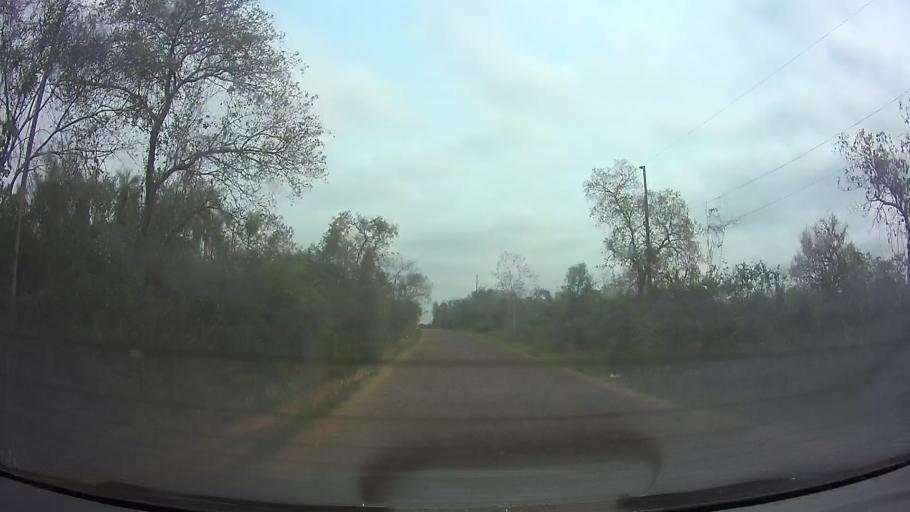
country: PY
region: Cordillera
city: Arroyos y Esteros
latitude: -24.9868
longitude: -57.2059
